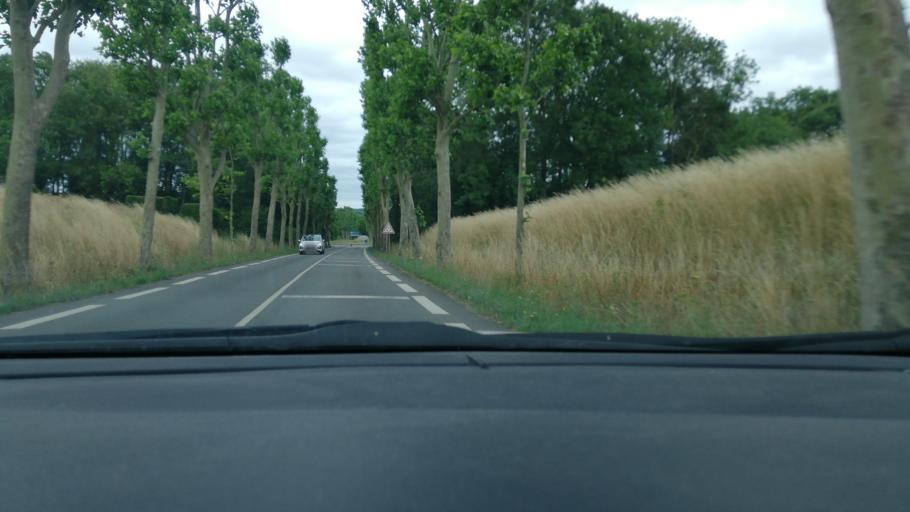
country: FR
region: Ile-de-France
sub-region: Departement du Val-d'Oise
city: Auvers-sur-Oise
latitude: 49.0799
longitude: 2.1576
